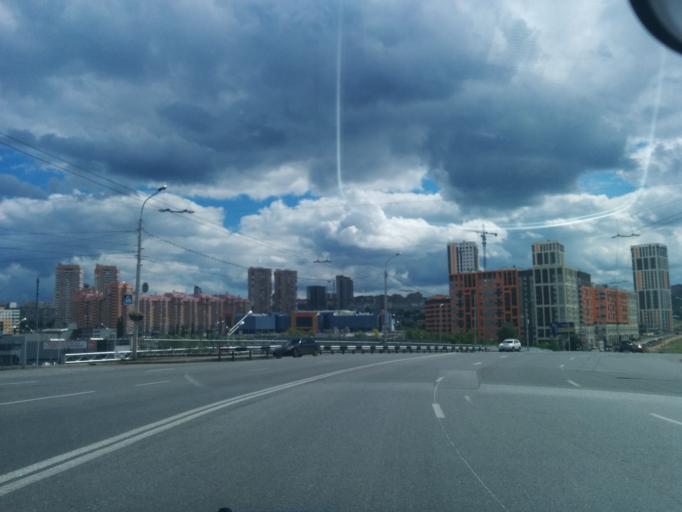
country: RU
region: Bashkortostan
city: Ufa
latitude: 54.7212
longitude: 55.9769
